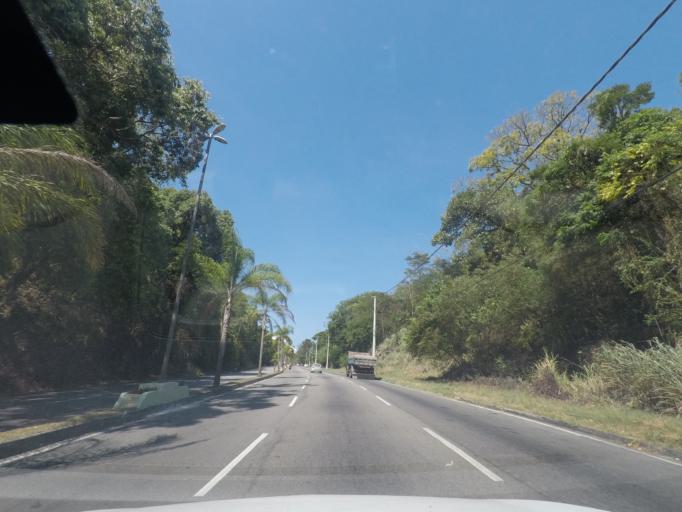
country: BR
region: Rio de Janeiro
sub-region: Niteroi
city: Niteroi
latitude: -22.9230
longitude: -43.0569
